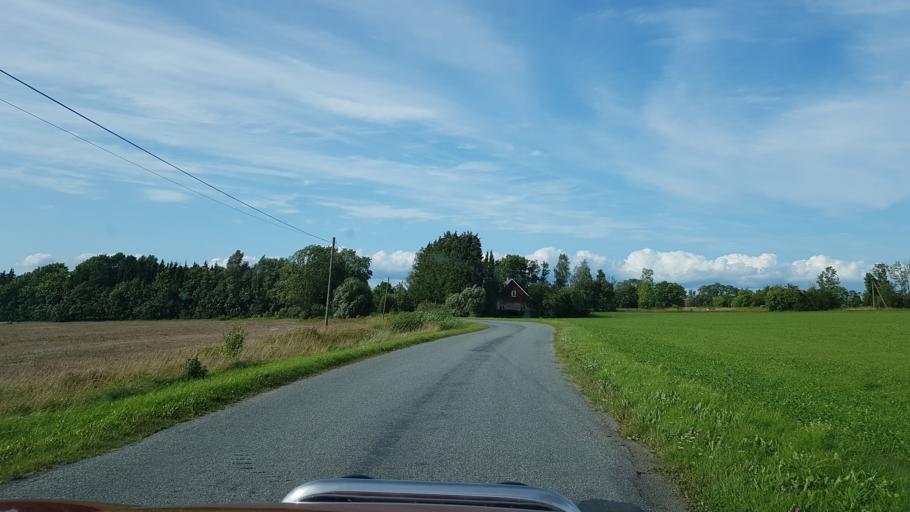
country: EE
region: Laeaene
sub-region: Lihula vald
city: Lihula
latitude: 58.4421
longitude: 24.0034
